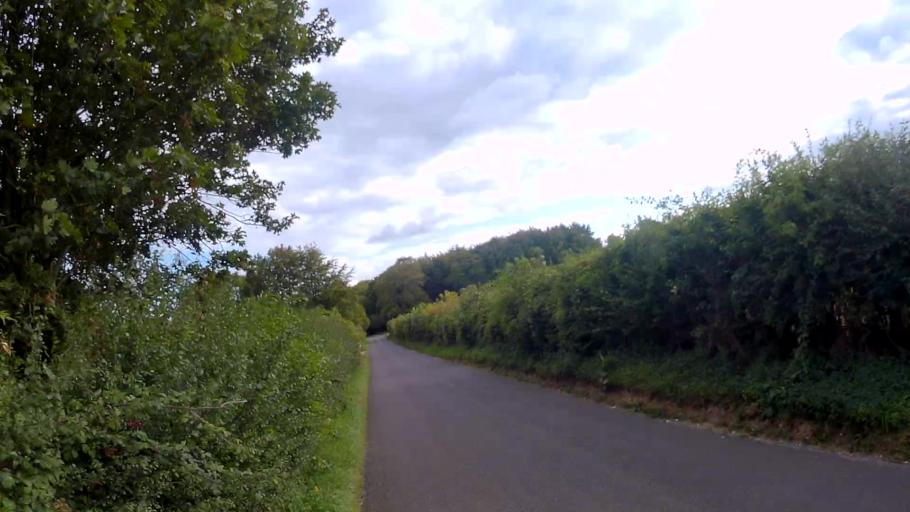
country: GB
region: England
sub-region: Hampshire
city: Kings Worthy
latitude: 51.1349
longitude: -1.2108
